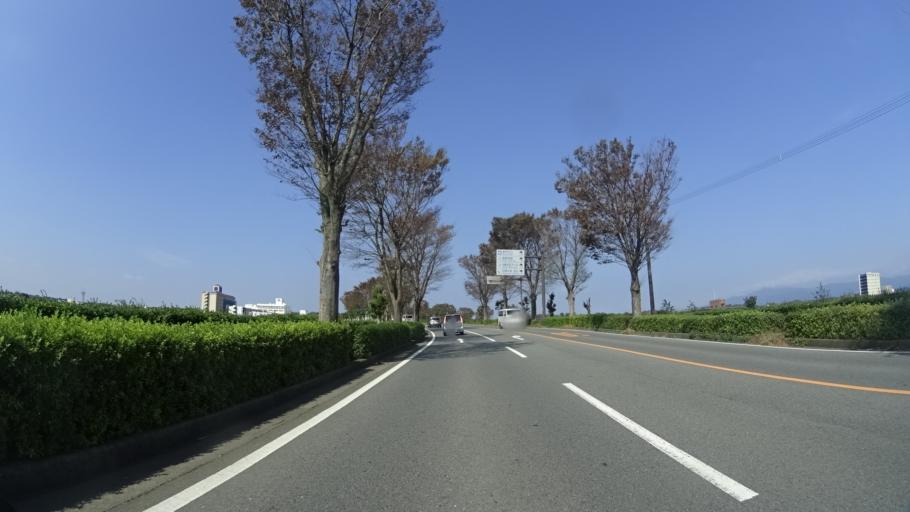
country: JP
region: Kumamoto
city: Ozu
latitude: 32.8724
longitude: 130.8552
